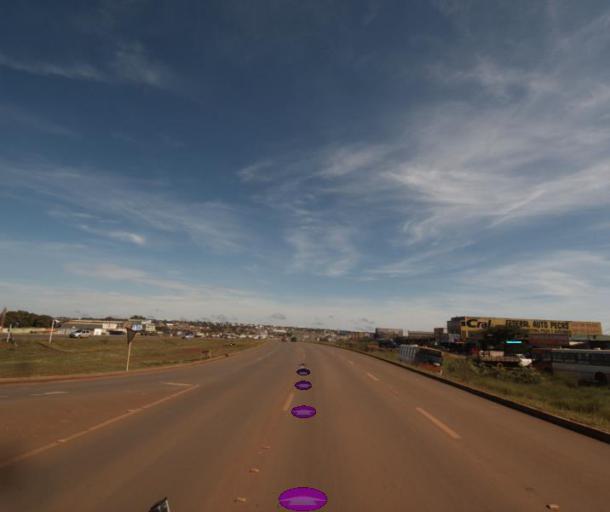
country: BR
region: Federal District
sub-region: Brasilia
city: Brasilia
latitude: -15.7488
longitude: -48.2627
